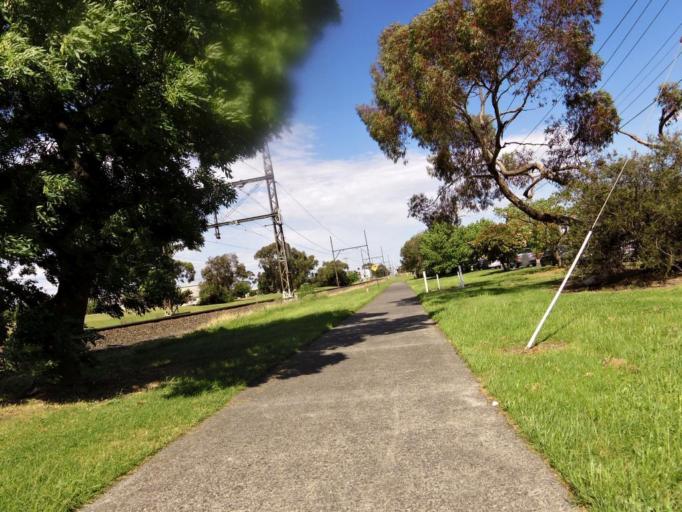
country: AU
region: Victoria
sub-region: Kingston
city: Clayton South
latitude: -37.9279
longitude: 145.1247
